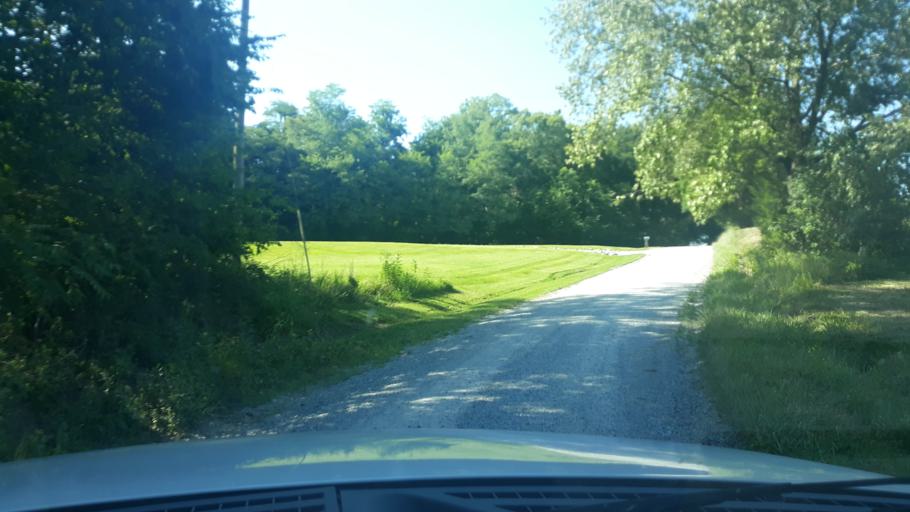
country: US
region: Illinois
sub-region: Saline County
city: Eldorado
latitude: 37.8396
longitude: -88.4936
